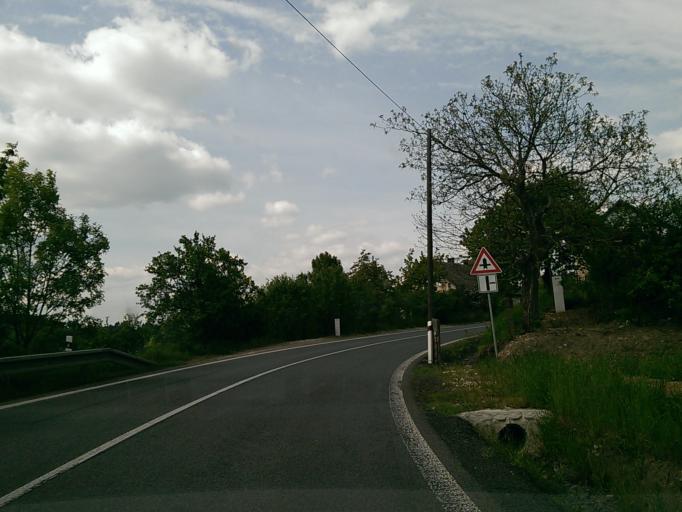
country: CZ
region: Liberecky
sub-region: Okres Semily
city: Turnov
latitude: 50.6071
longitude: 15.1645
